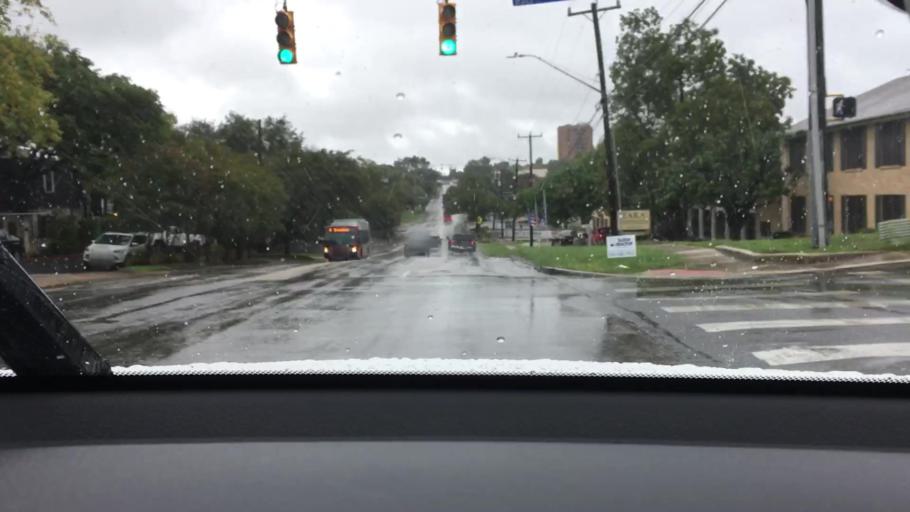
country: US
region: Texas
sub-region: Bexar County
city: Alamo Heights
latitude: 29.5098
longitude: -98.4662
